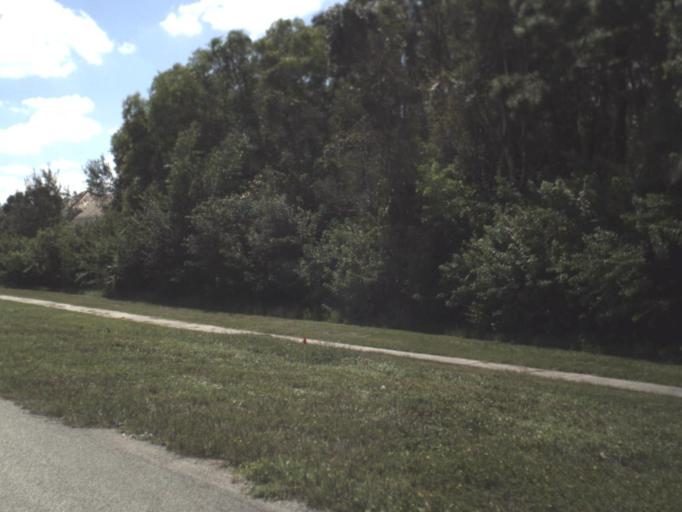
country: US
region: Florida
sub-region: Lee County
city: San Carlos Park
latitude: 26.4661
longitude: -81.8329
